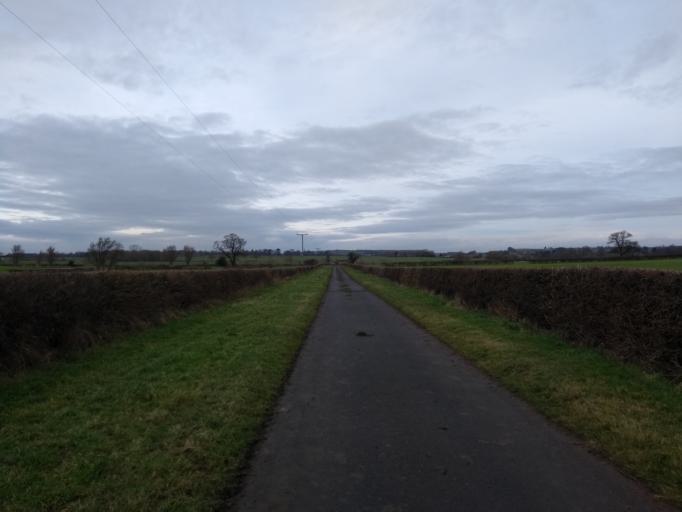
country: GB
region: England
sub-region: East Riding of Yorkshire
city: Stamford Bridge
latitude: 54.0648
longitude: -0.9307
